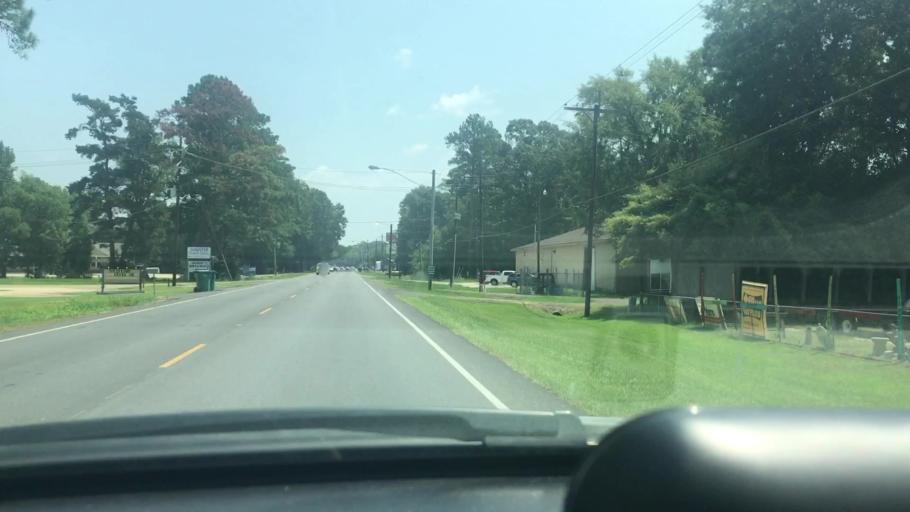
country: US
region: Louisiana
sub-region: Livingston Parish
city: Walker
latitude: 30.4875
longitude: -90.8679
